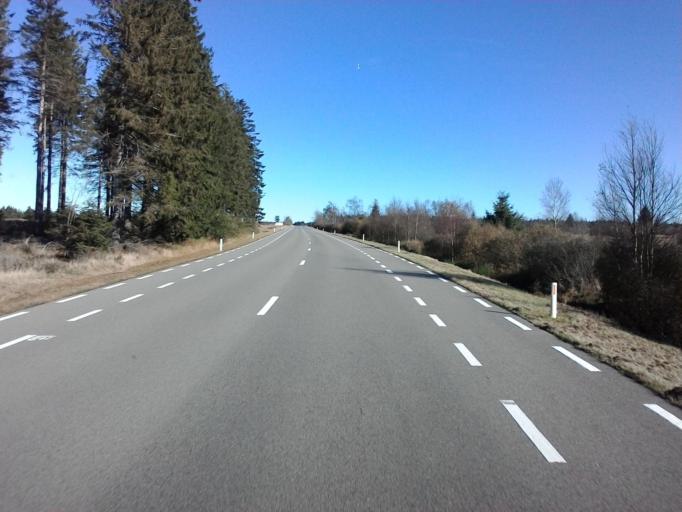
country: BE
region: Wallonia
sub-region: Province de Liege
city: Malmedy
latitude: 50.4966
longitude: 6.0709
